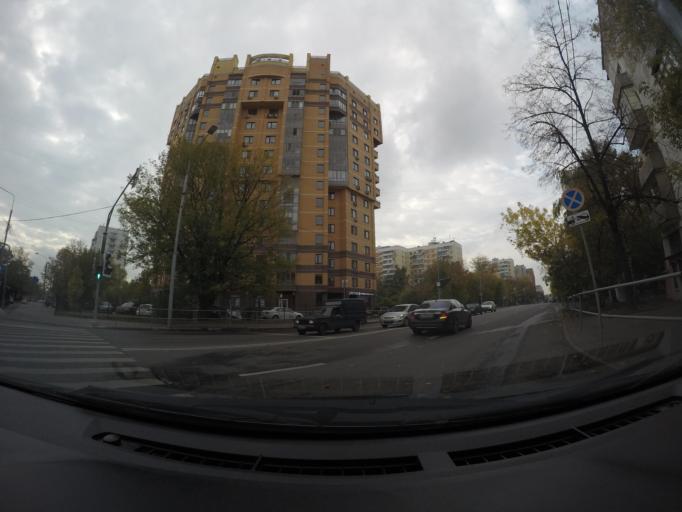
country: RU
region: Moskovskaya
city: Novogireyevo
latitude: 55.7546
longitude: 37.8179
